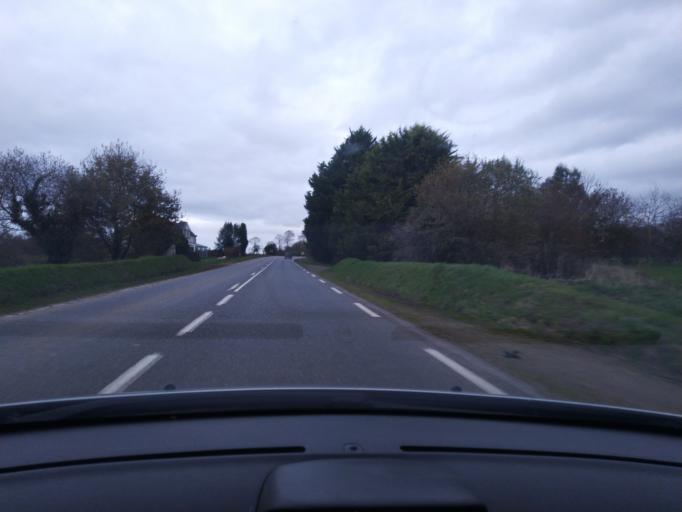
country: FR
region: Brittany
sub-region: Departement des Cotes-d'Armor
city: Plouaret
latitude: 48.5923
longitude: -3.4954
